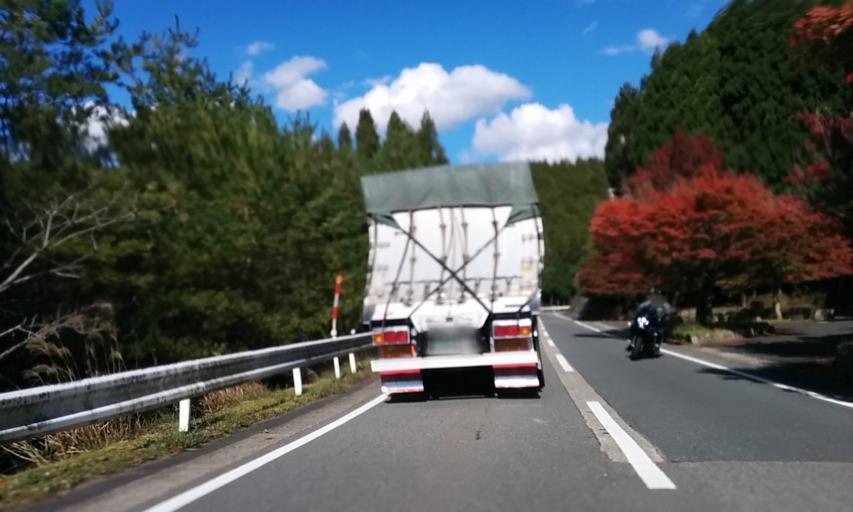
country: JP
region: Kyoto
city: Kameoka
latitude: 35.2029
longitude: 135.6169
